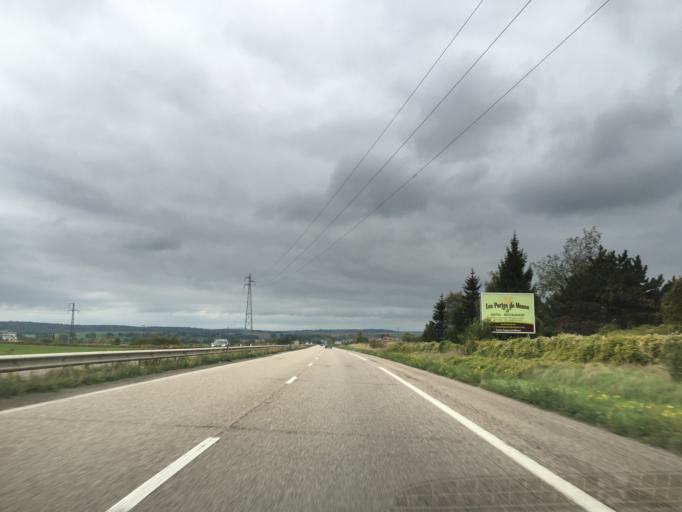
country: FR
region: Lorraine
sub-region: Departement de Meurthe-et-Moselle
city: Foug
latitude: 48.6818
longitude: 5.7431
